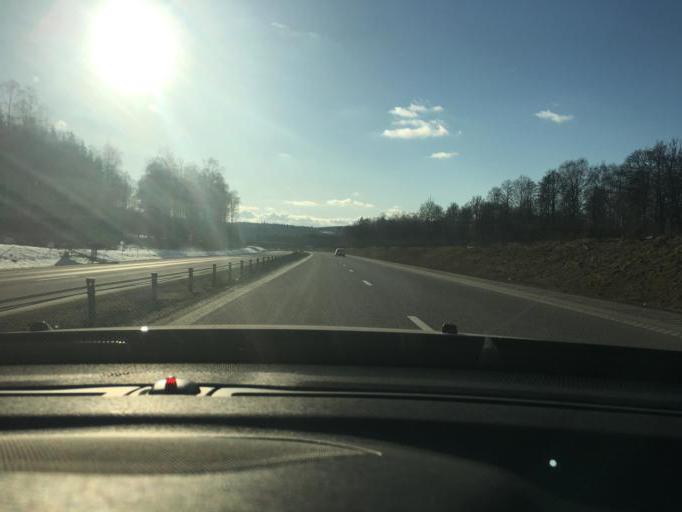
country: SE
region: Vaestra Goetaland
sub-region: Boras Kommun
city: Dalsjofors
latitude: 57.7959
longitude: 13.1469
